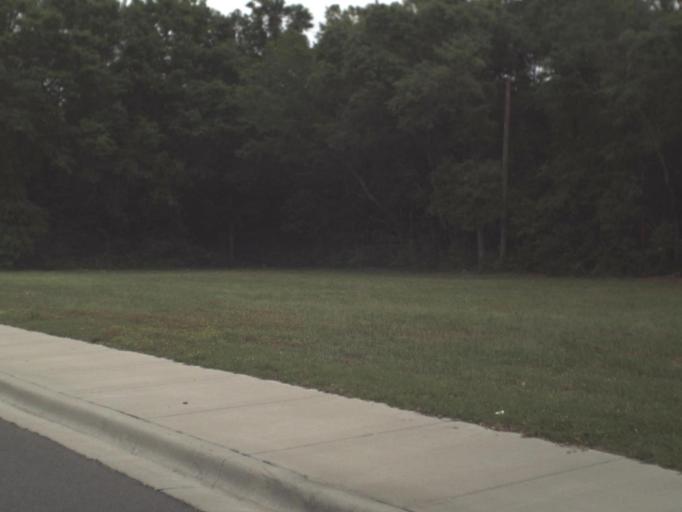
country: US
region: Florida
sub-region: Santa Rosa County
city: Bagdad
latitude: 30.5883
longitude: -87.0851
